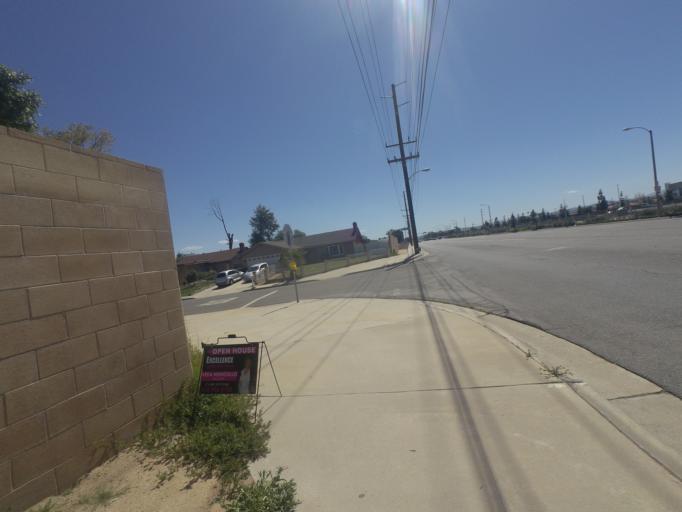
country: US
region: California
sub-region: Riverside County
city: Moreno Valley
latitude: 33.9125
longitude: -117.2435
